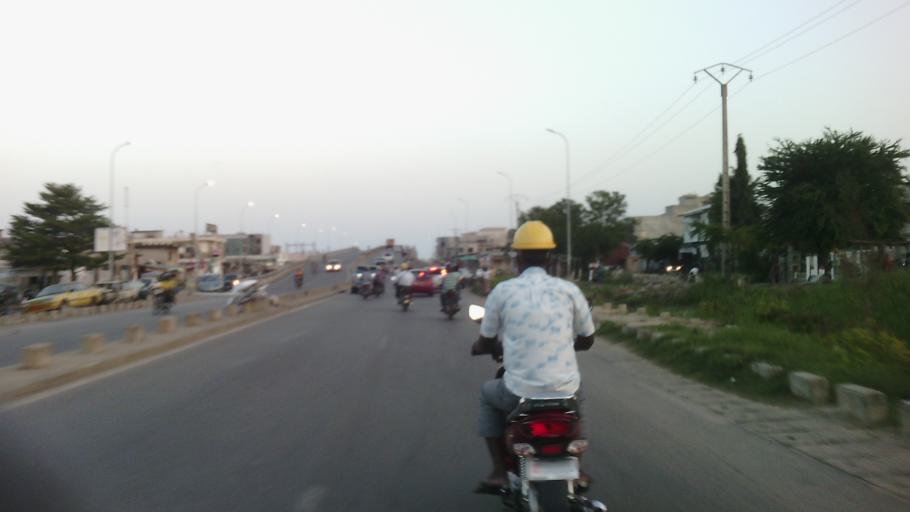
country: BJ
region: Littoral
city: Cotonou
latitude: 6.3710
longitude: 2.3936
